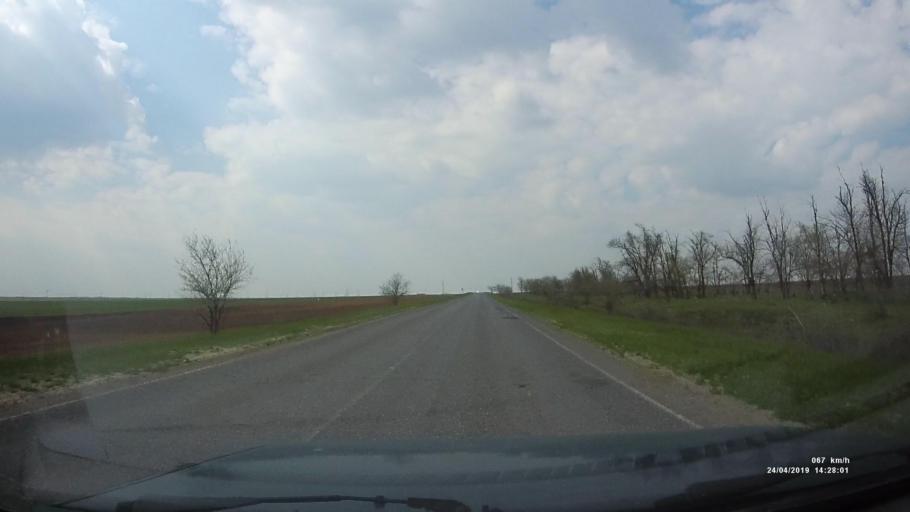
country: RU
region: Kalmykiya
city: Arshan'
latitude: 46.3354
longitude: 44.0339
